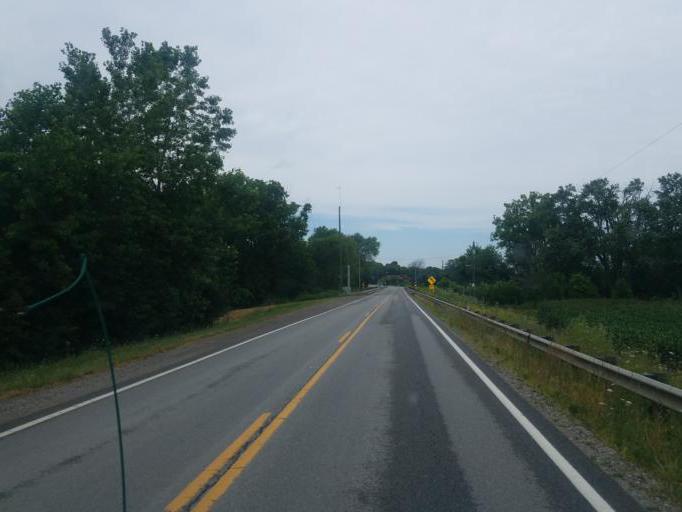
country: US
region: Ohio
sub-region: Williams County
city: Edgerton
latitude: 41.3853
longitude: -84.8008
